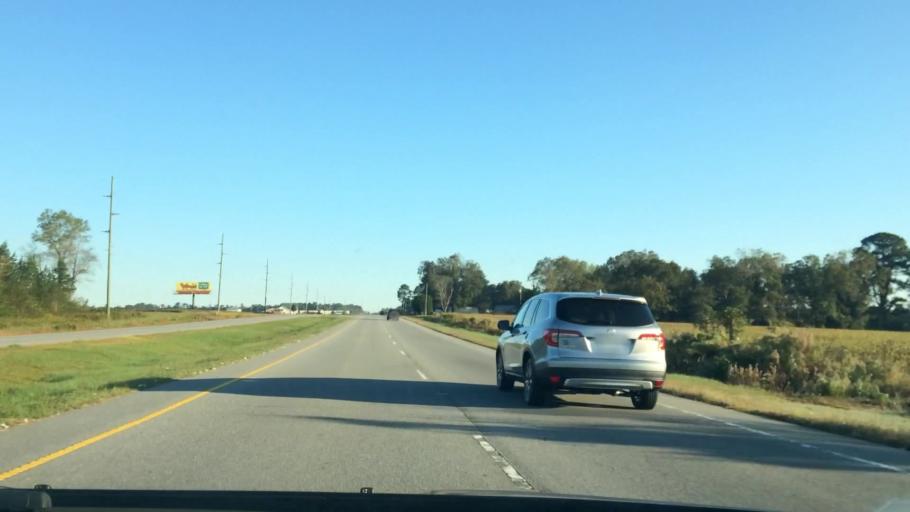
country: US
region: North Carolina
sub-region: Pitt County
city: Ayden
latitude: 35.4338
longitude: -77.4331
